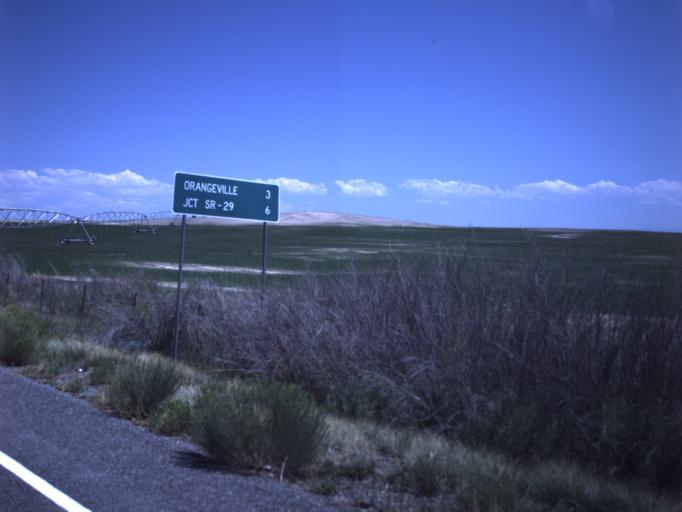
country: US
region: Utah
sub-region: Emery County
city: Castle Dale
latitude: 39.1804
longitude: -111.0476
